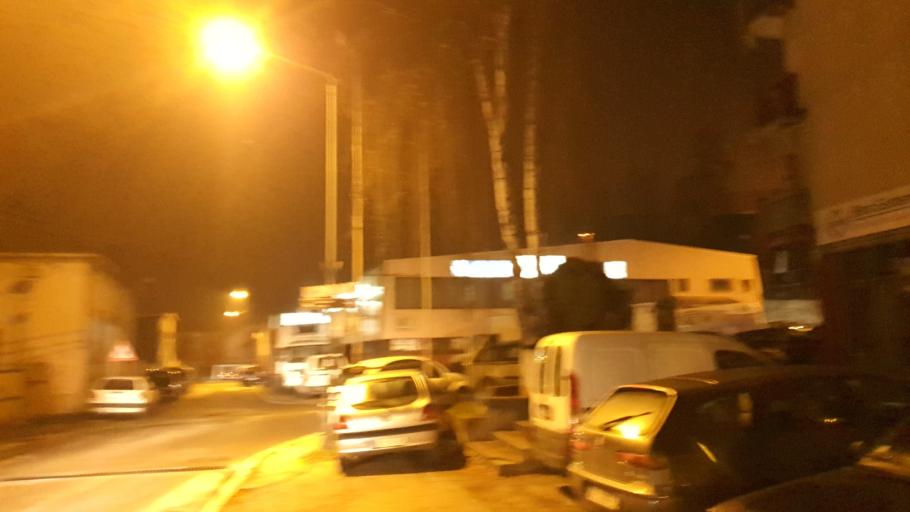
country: RS
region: Central Serbia
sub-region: Zlatiborski Okrug
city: Uzice
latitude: 43.8557
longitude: 19.8355
